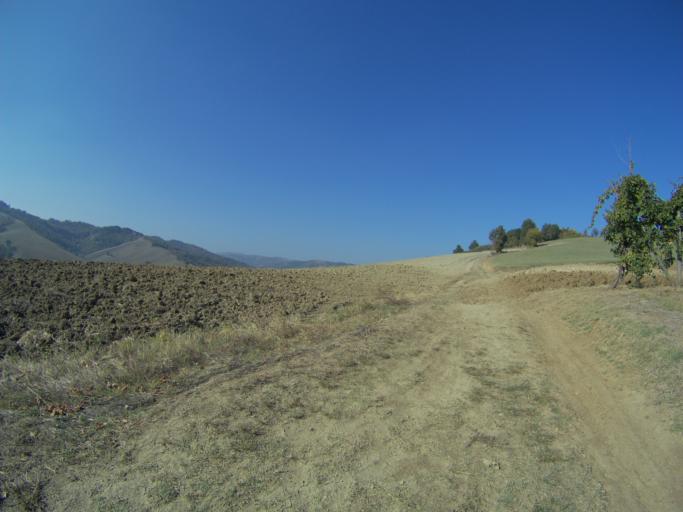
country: IT
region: Emilia-Romagna
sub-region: Provincia di Reggio Emilia
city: Vezzano sul Crostolo
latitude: 44.6103
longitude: 10.5373
